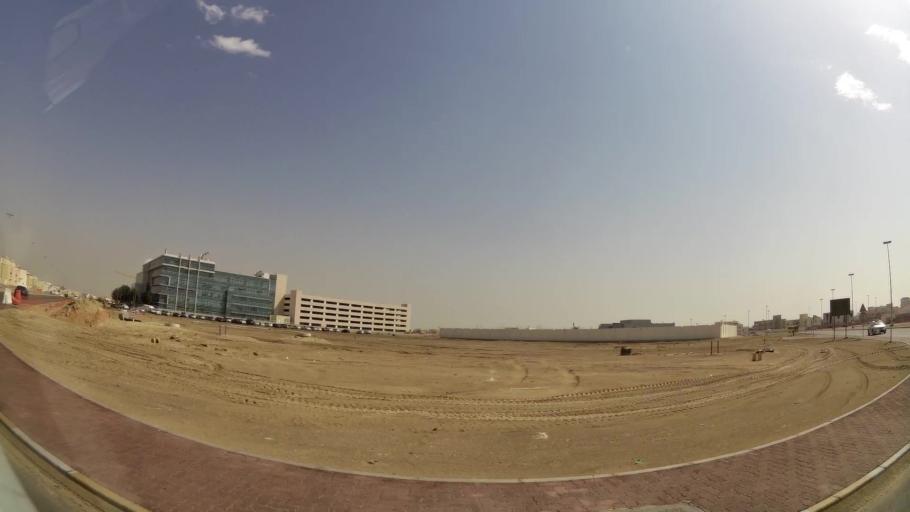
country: AE
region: Abu Dhabi
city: Abu Dhabi
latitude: 24.3185
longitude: 54.5509
